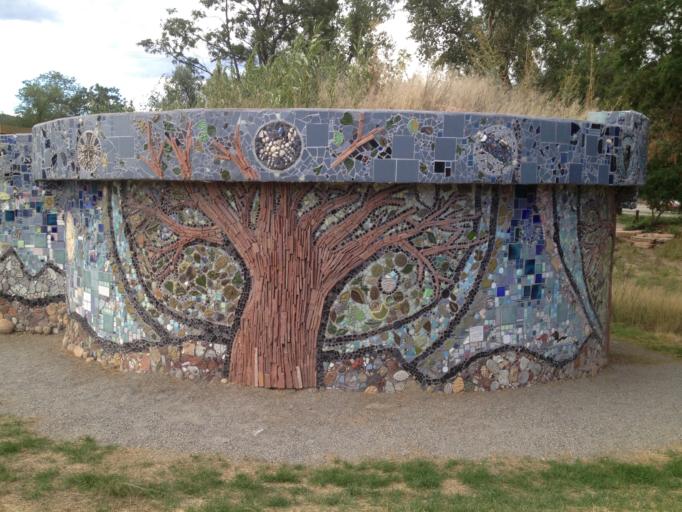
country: US
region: Colorado
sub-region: Boulder County
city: Lyons
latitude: 40.2201
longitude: -105.2635
